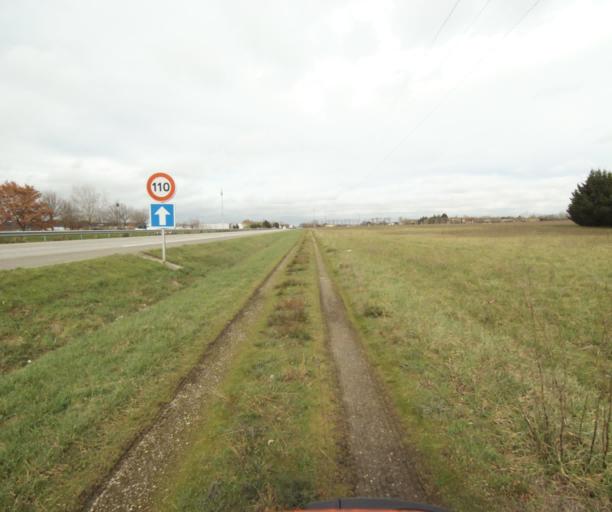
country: FR
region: Midi-Pyrenees
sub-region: Departement de l'Ariege
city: La Tour-du-Crieu
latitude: 43.1085
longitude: 1.6321
